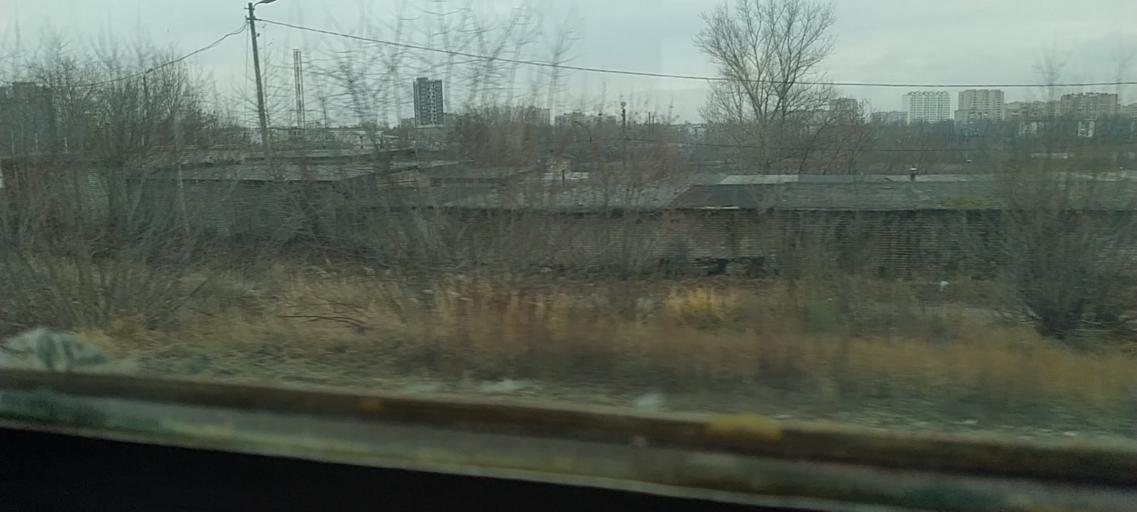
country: RU
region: Moskovskaya
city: Korenevo
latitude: 55.6691
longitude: 37.9889
